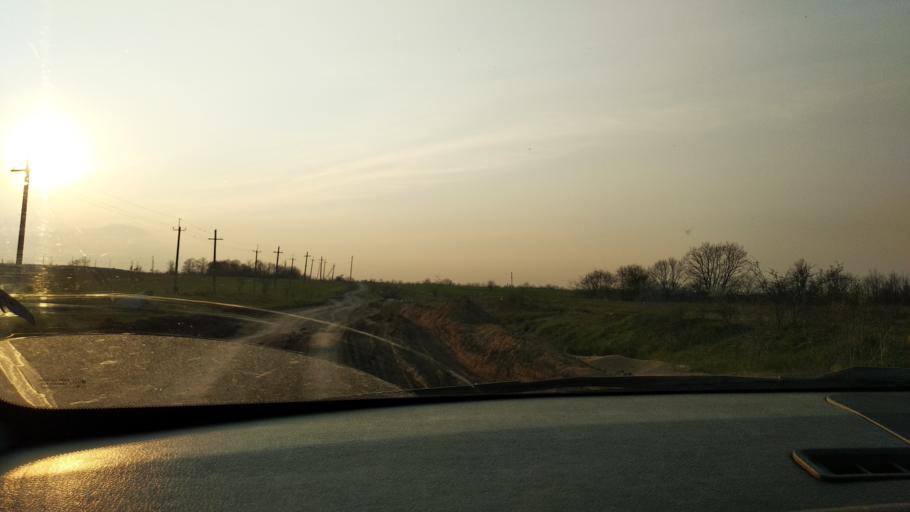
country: RU
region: Adygeya
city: Adygeysk
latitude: 44.8269
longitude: 39.2325
